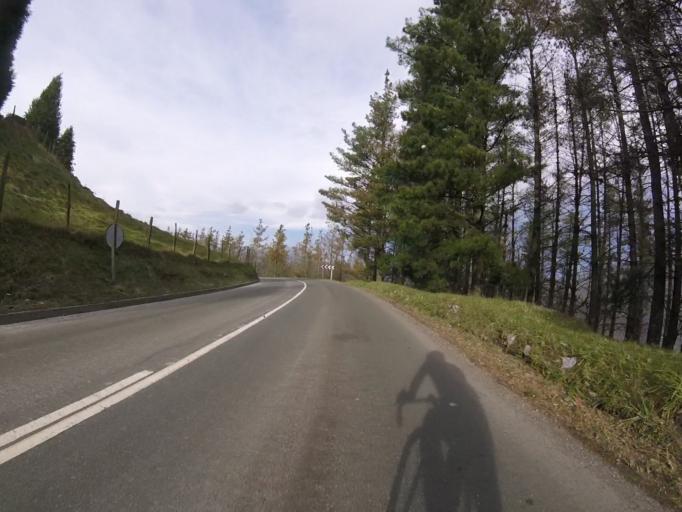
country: ES
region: Basque Country
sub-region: Provincia de Guipuzcoa
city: Beizama
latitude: 43.1521
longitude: -2.1908
